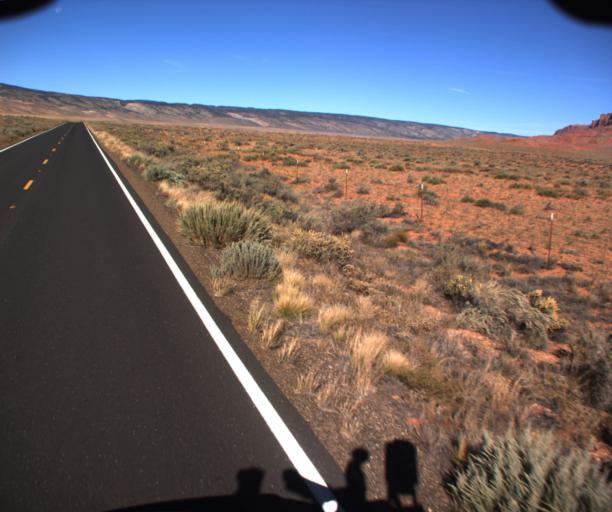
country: US
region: Arizona
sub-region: Coconino County
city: Page
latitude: 36.7151
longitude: -111.9909
